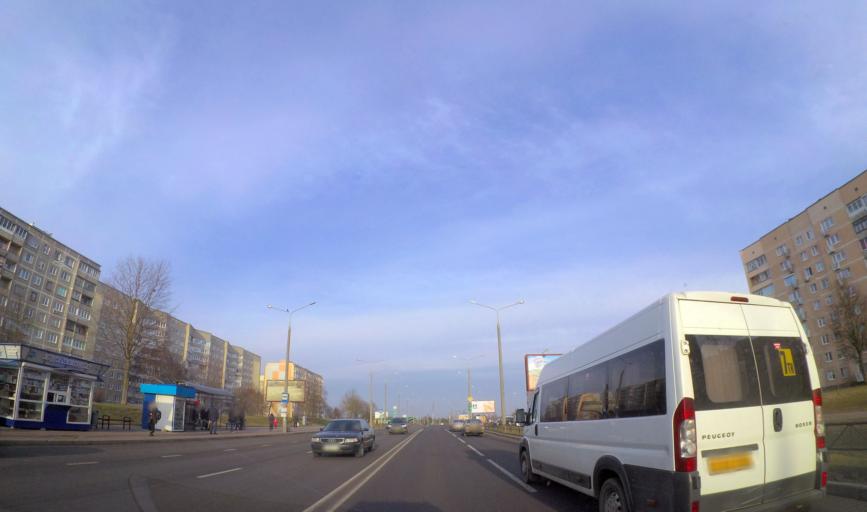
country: BY
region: Grodnenskaya
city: Hrodna
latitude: 53.6624
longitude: 23.7833
